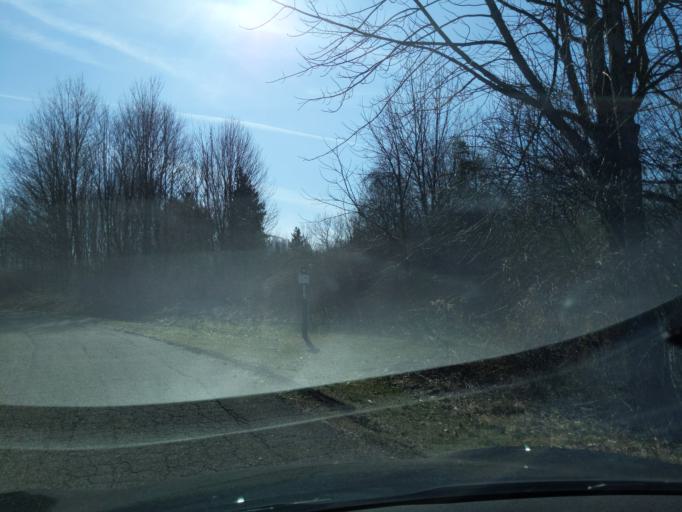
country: US
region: Michigan
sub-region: Ionia County
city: Ionia
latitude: 42.9381
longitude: -85.1311
